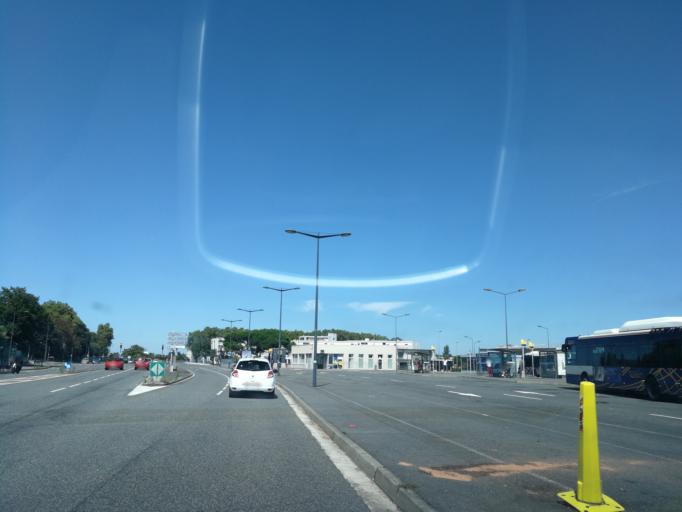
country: FR
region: Midi-Pyrenees
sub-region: Departement de la Haute-Garonne
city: Ramonville-Saint-Agne
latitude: 43.5600
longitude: 1.4633
